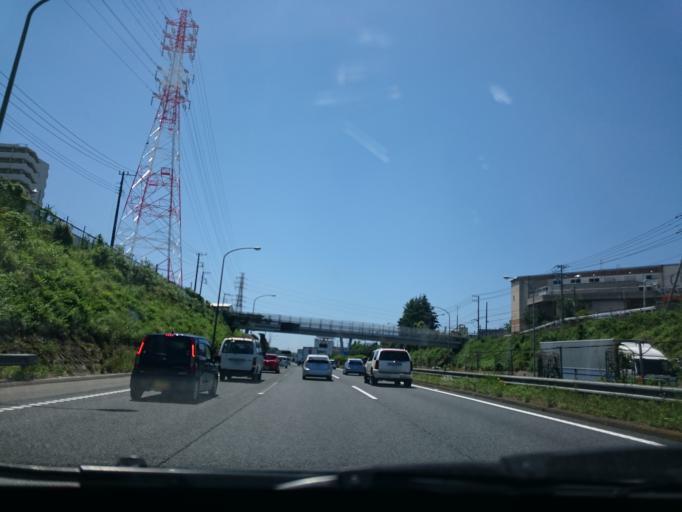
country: JP
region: Kanagawa
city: Minami-rinkan
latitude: 35.4979
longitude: 139.4749
